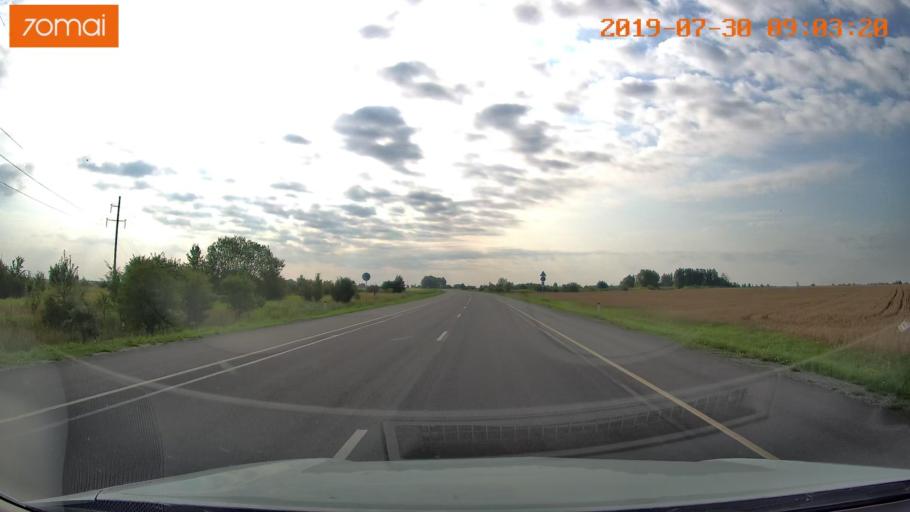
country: RU
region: Kaliningrad
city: Gusev
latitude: 54.6087
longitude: 22.2509
